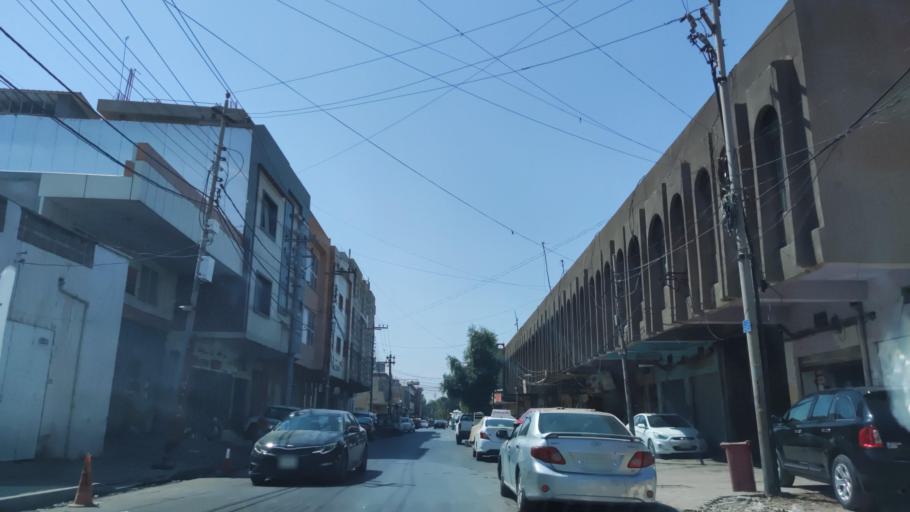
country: IQ
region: Arbil
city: Erbil
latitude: 36.1880
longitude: 44.0221
